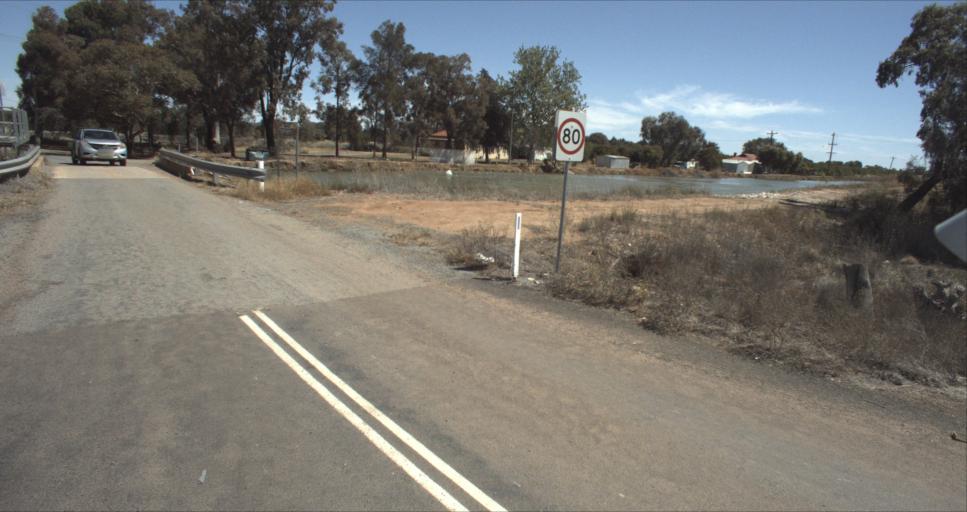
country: AU
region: New South Wales
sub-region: Leeton
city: Leeton
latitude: -34.5242
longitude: 146.3459
